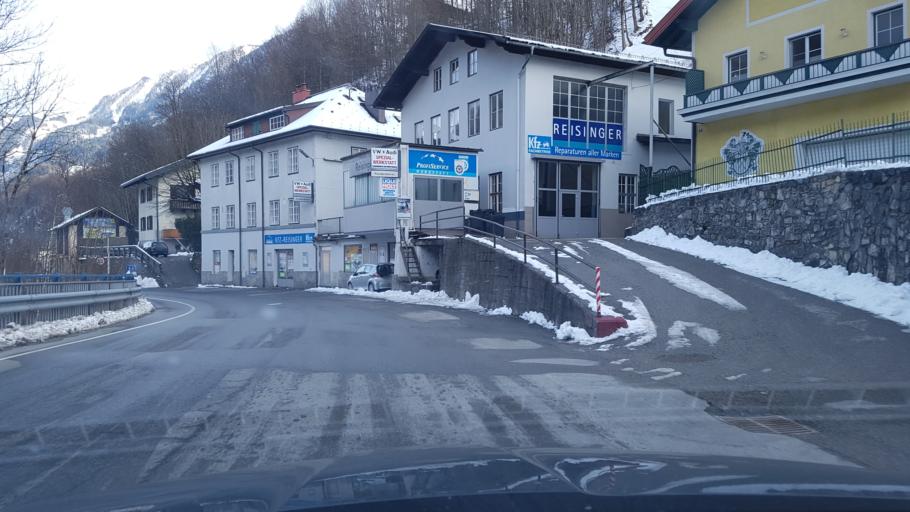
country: AT
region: Salzburg
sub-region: Politischer Bezirk Zell am See
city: Lend
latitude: 47.2968
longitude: 13.0513
